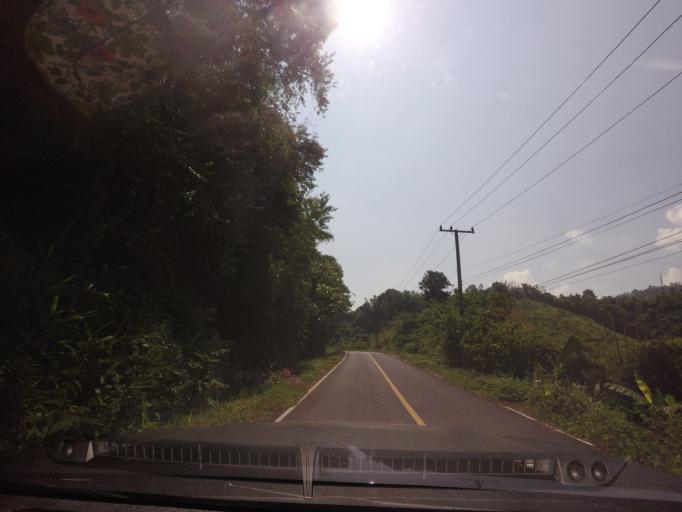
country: TH
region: Nan
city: Bo Kluea
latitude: 19.0299
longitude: 101.1758
